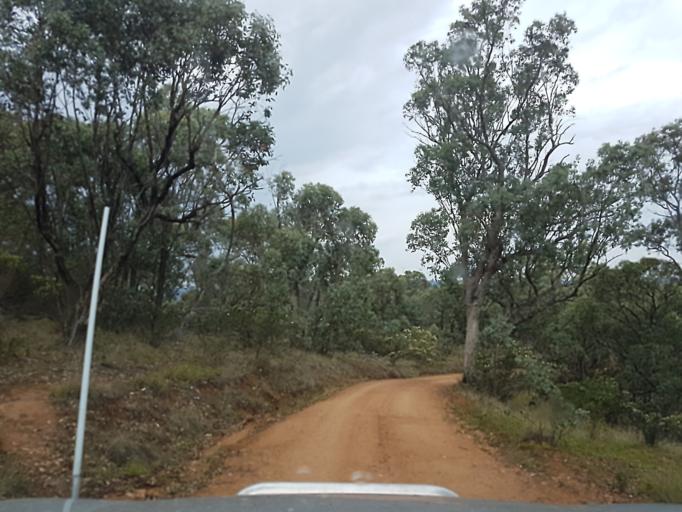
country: AU
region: New South Wales
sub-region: Snowy River
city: Jindabyne
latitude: -36.9557
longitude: 148.3619
